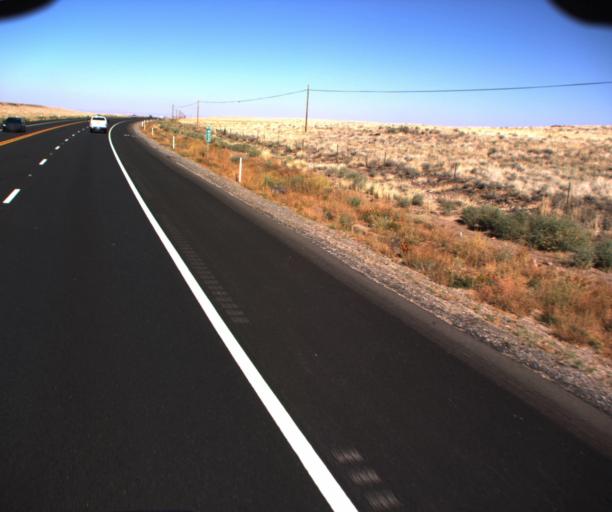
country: US
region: Arizona
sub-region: Coconino County
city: Flagstaff
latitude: 35.6903
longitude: -111.5045
